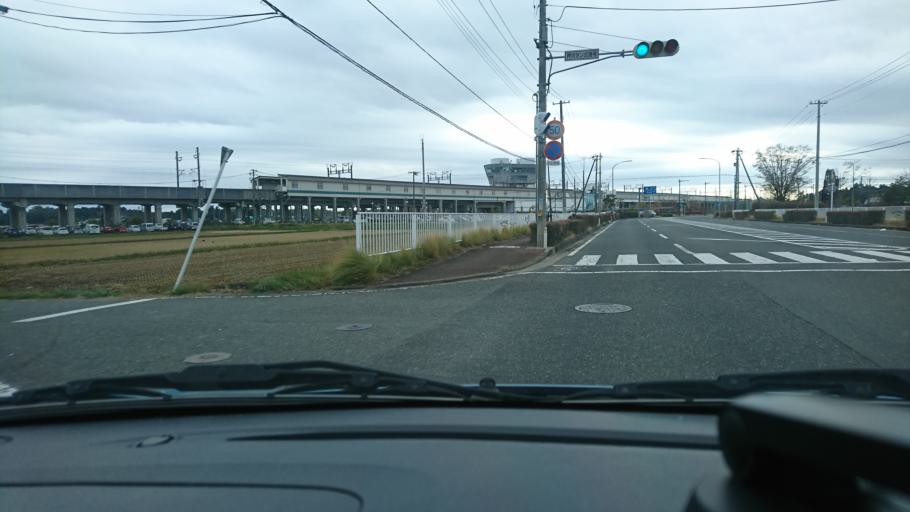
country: JP
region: Iwate
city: Ichinoseki
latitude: 38.7517
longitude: 141.0715
